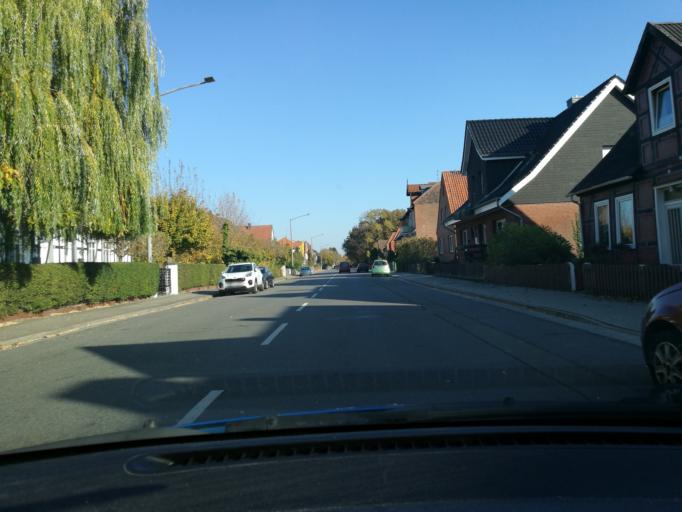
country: DE
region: Lower Saxony
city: Dannenberg
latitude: 53.1030
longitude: 11.1112
